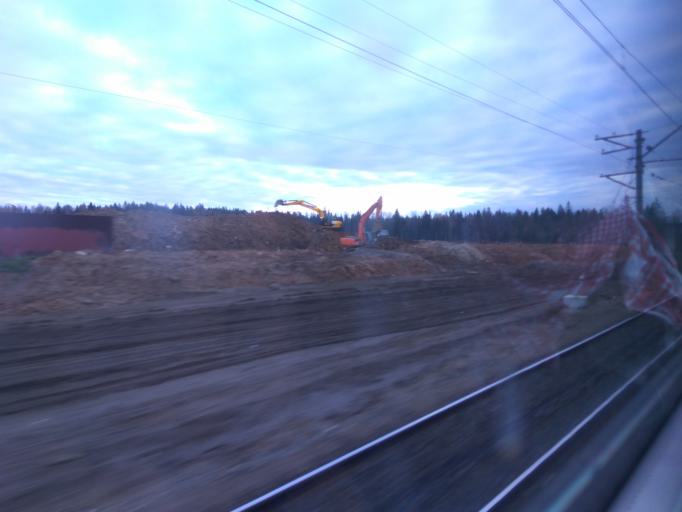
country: RU
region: Moskovskaya
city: Selyatino
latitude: 55.5126
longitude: 36.9607
